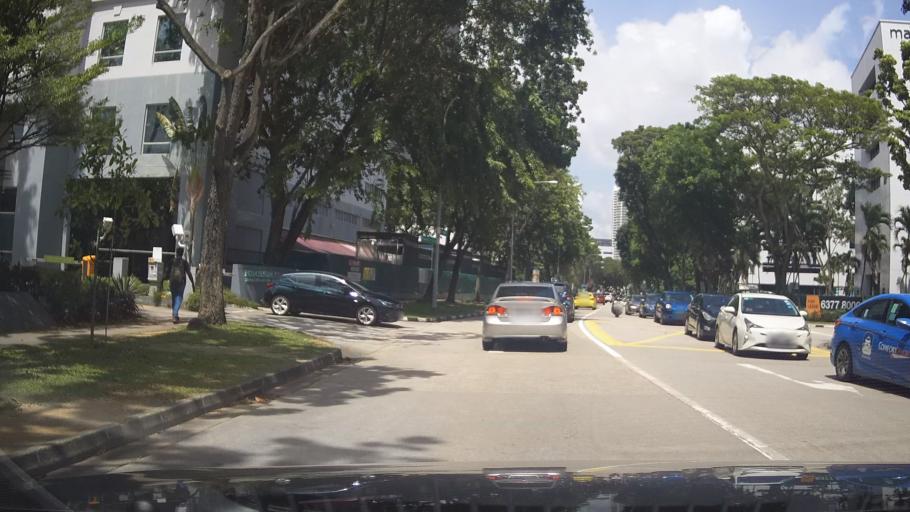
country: SG
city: Singapore
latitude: 1.3098
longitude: 103.8653
